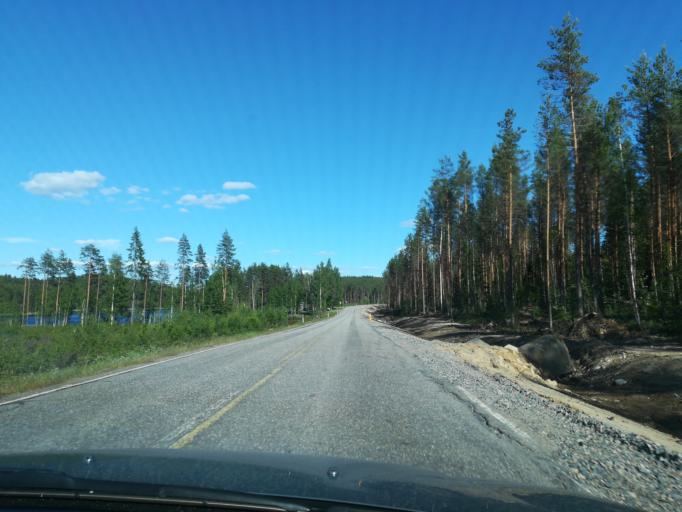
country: FI
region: Southern Savonia
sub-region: Mikkeli
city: Puumala
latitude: 61.4644
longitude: 28.3841
